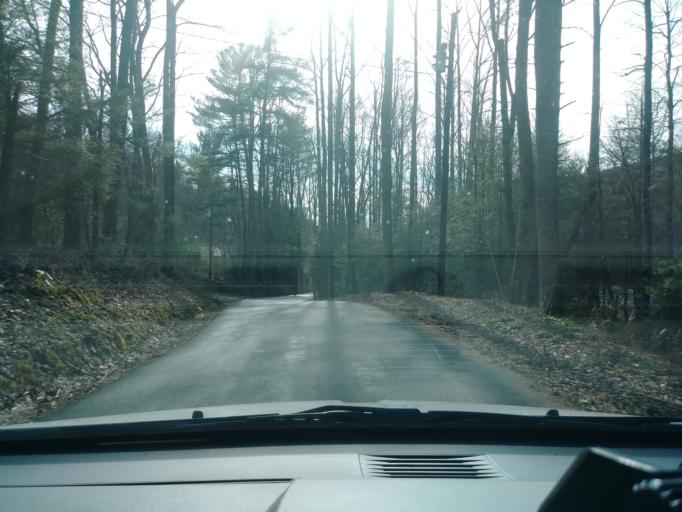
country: US
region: Tennessee
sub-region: Greene County
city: Tusculum
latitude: 36.0241
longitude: -82.7378
